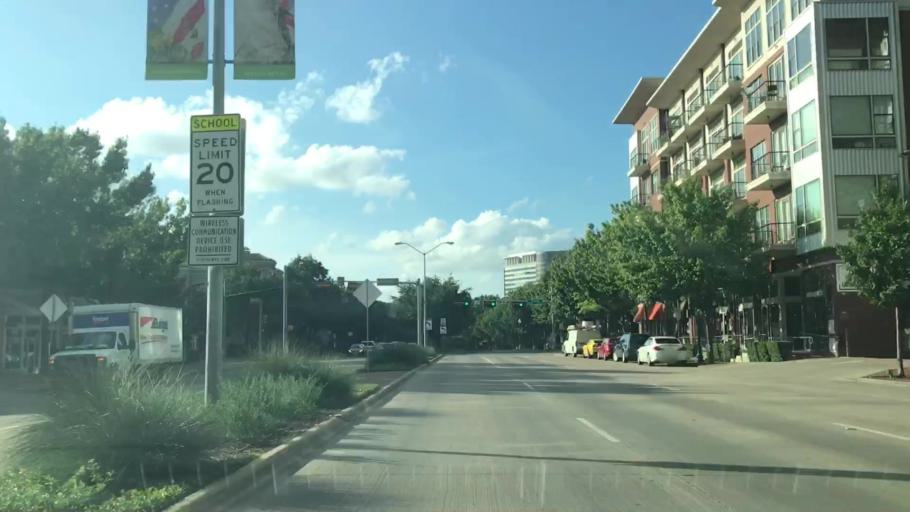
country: US
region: Texas
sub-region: Dallas County
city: Highland Park
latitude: 32.8090
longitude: -96.7961
